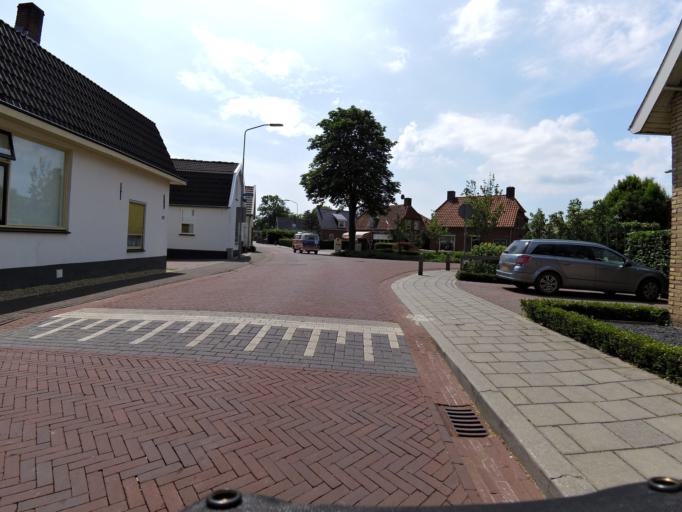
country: NL
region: North Brabant
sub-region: Gemeente Aalburg
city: Aalburg
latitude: 51.8174
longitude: 5.0916
